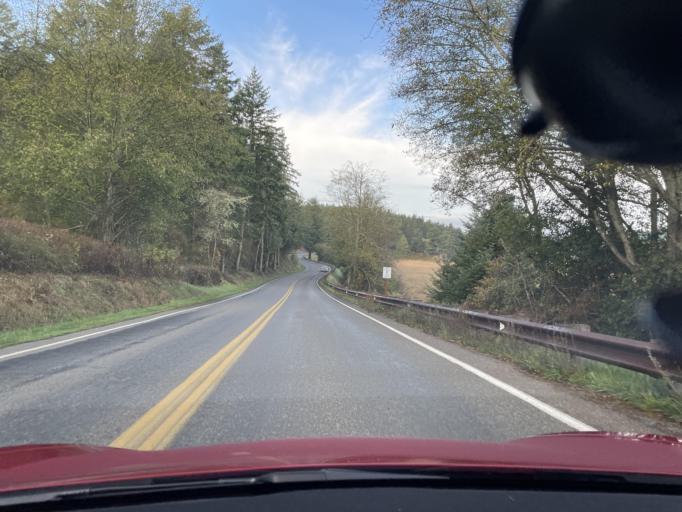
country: US
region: Washington
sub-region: San Juan County
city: Friday Harbor
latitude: 48.5398
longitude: -123.0414
